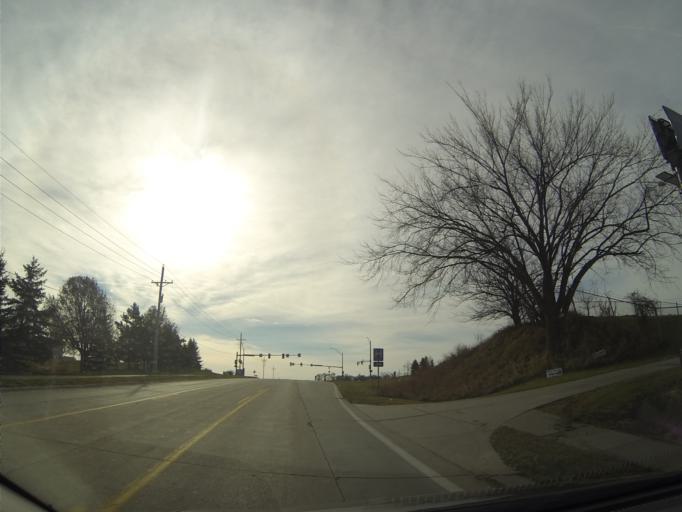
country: US
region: Nebraska
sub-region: Douglas County
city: Elkhorn
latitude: 41.2676
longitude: -96.2156
